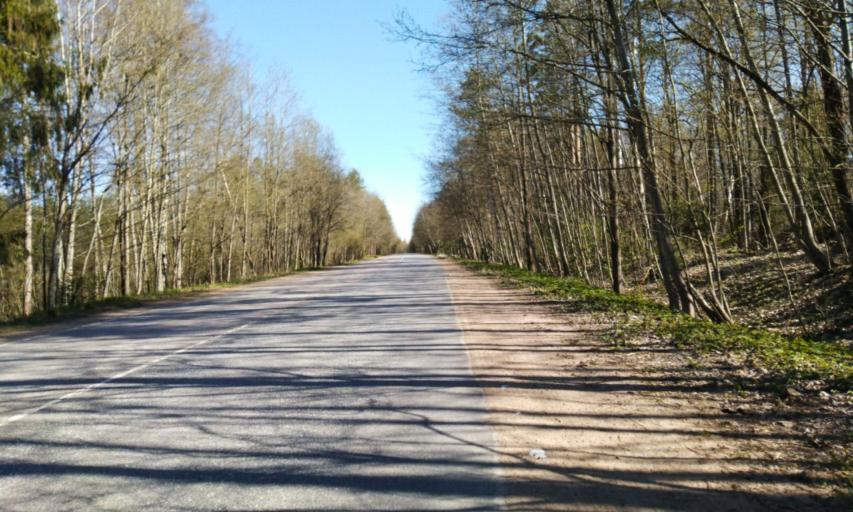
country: RU
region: Leningrad
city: Garbolovo
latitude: 60.3872
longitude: 30.4751
